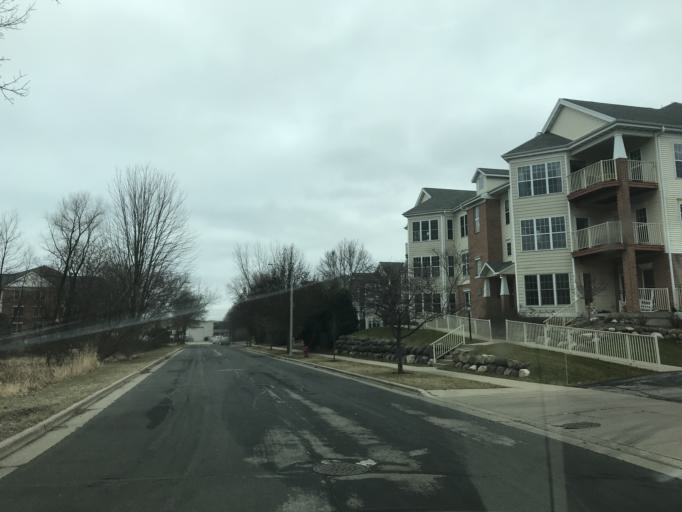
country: US
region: Wisconsin
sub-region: Dane County
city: Monona
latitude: 43.0523
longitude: -89.3132
